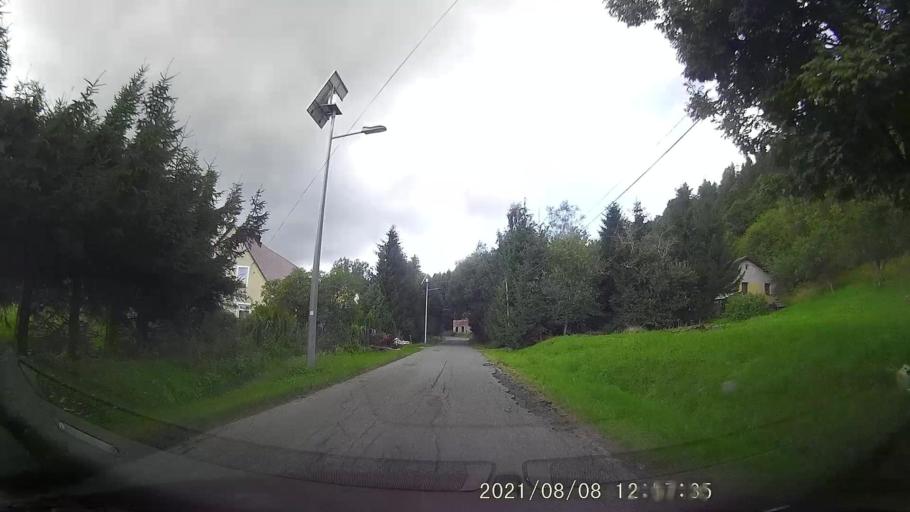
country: PL
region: Lower Silesian Voivodeship
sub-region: Powiat klodzki
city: Duszniki-Zdroj
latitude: 50.4103
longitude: 16.3673
